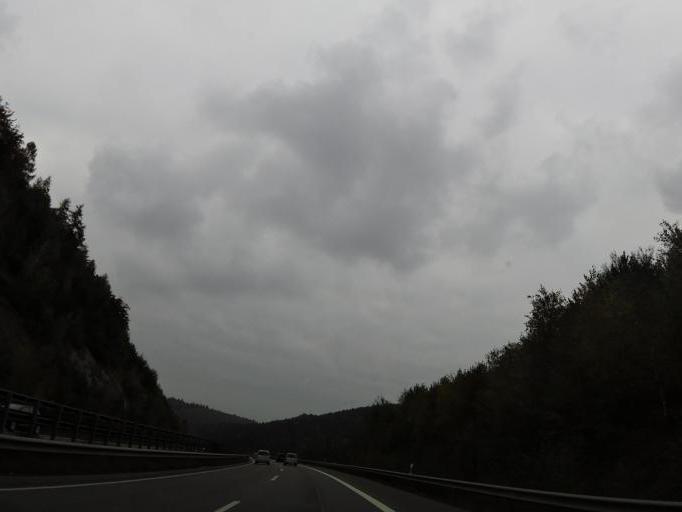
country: DE
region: Rheinland-Pfalz
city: Mehlingen
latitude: 49.4632
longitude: 7.8229
